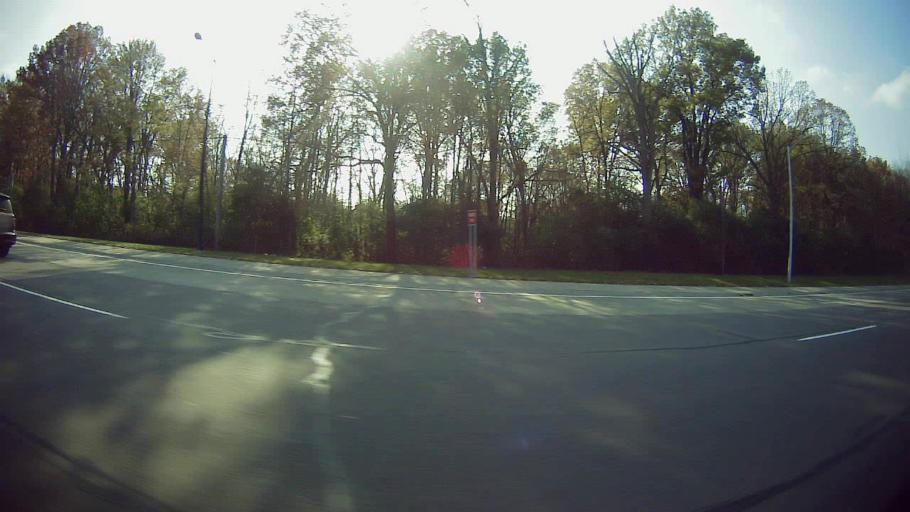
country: US
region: Michigan
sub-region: Wayne County
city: Dearborn Heights
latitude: 42.3286
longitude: -83.2307
